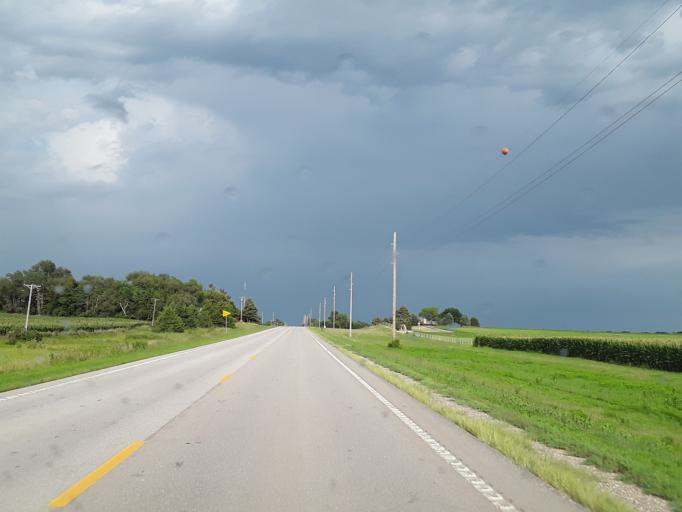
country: US
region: Nebraska
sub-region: Saunders County
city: Ashland
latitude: 41.0887
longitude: -96.4036
